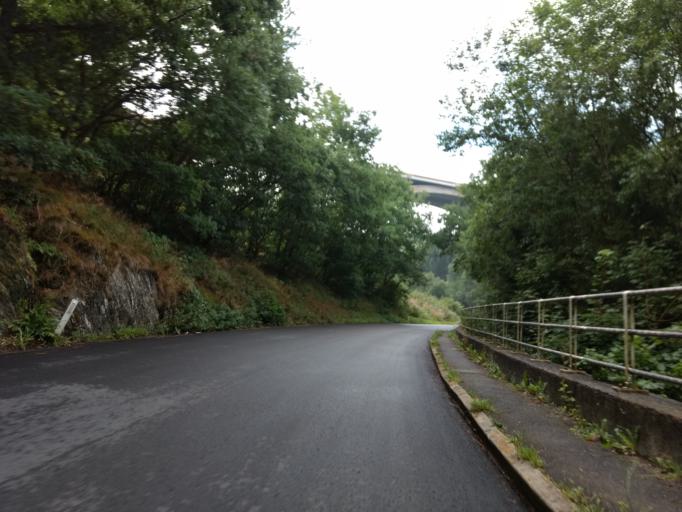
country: BE
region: Wallonia
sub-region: Province du Luxembourg
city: Houffalize
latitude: 50.1335
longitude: 5.7671
